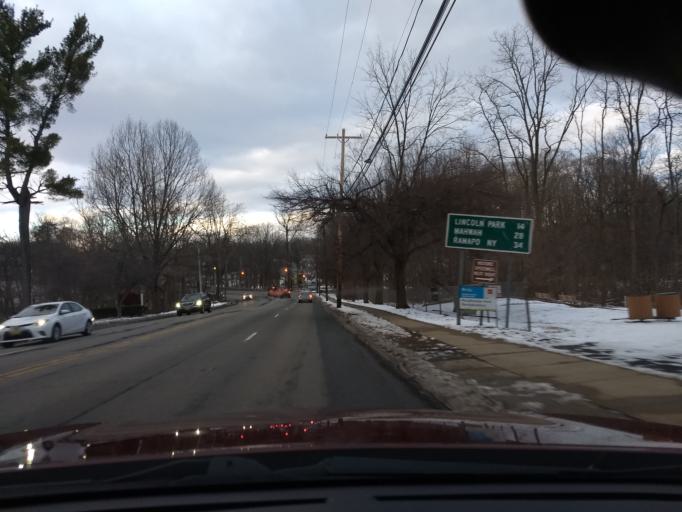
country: US
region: New Jersey
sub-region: Morris County
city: Morris Plains
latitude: 40.8116
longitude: -74.4804
